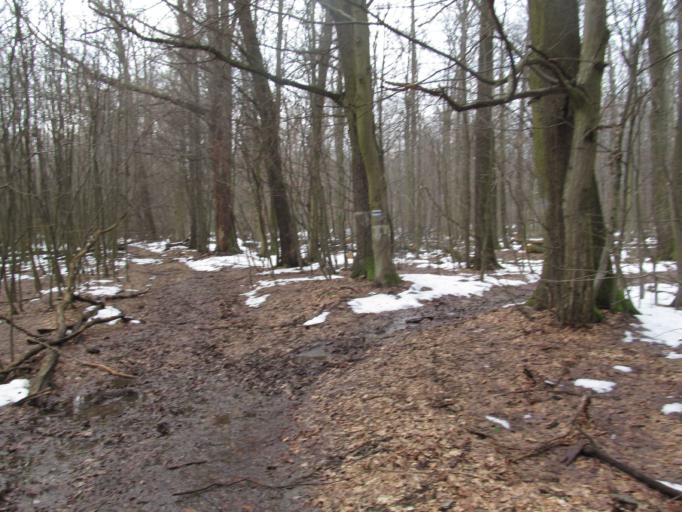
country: HU
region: Veszprem
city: Zirc
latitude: 47.2899
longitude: 17.7819
